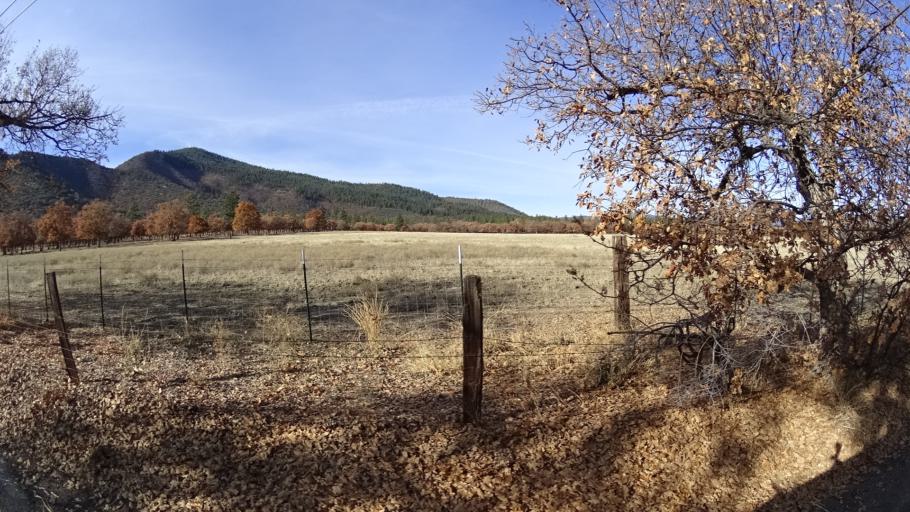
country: US
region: California
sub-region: Siskiyou County
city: Montague
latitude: 41.6480
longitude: -122.5829
